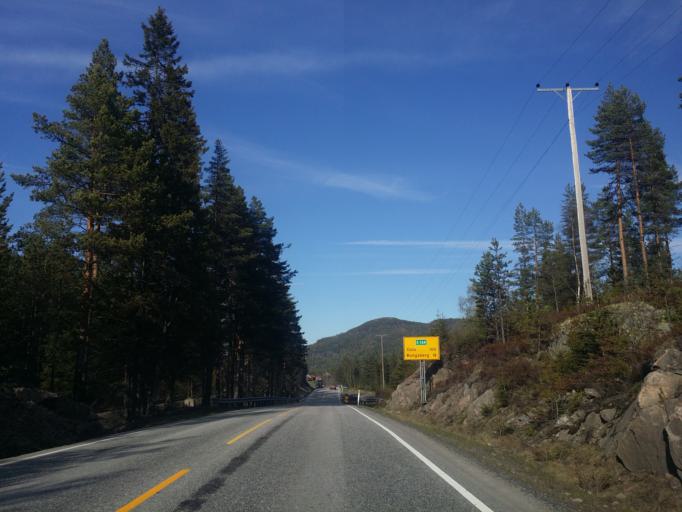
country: NO
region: Telemark
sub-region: Notodden
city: Notodden
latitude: 59.6078
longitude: 9.4433
